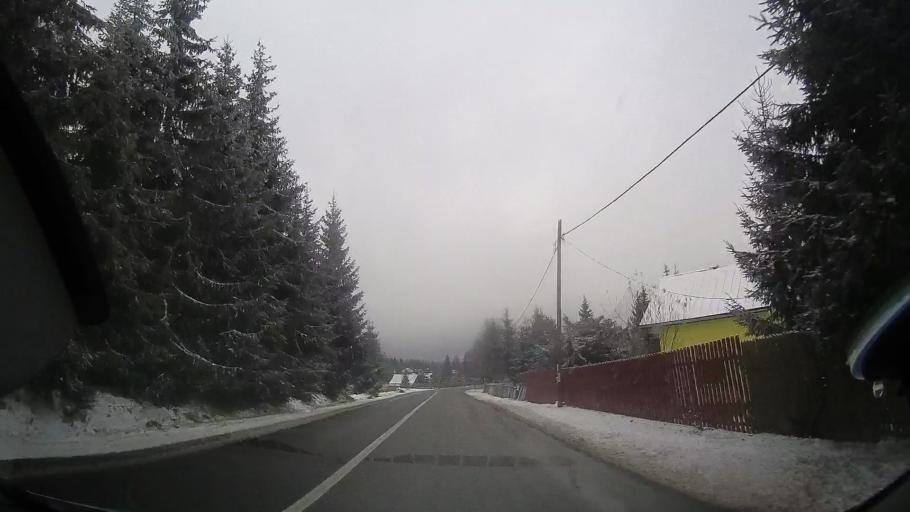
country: RO
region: Cluj
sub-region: Comuna Belis
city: Belis
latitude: 46.6804
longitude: 23.0385
